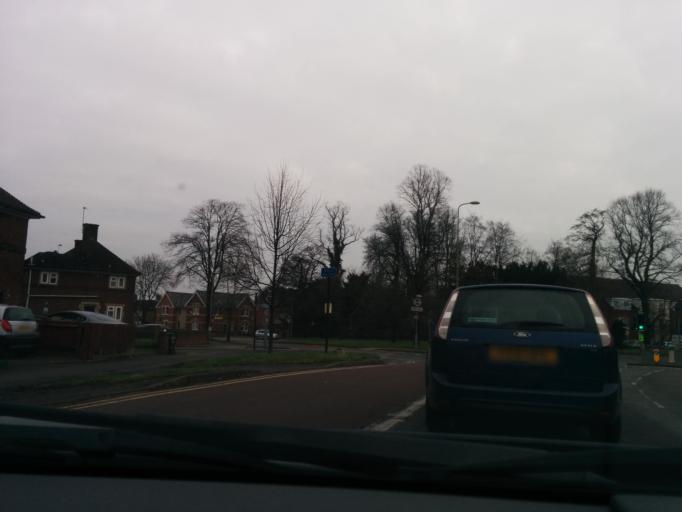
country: GB
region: England
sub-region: Oxfordshire
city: Oxford
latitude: 51.7315
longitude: -1.2496
